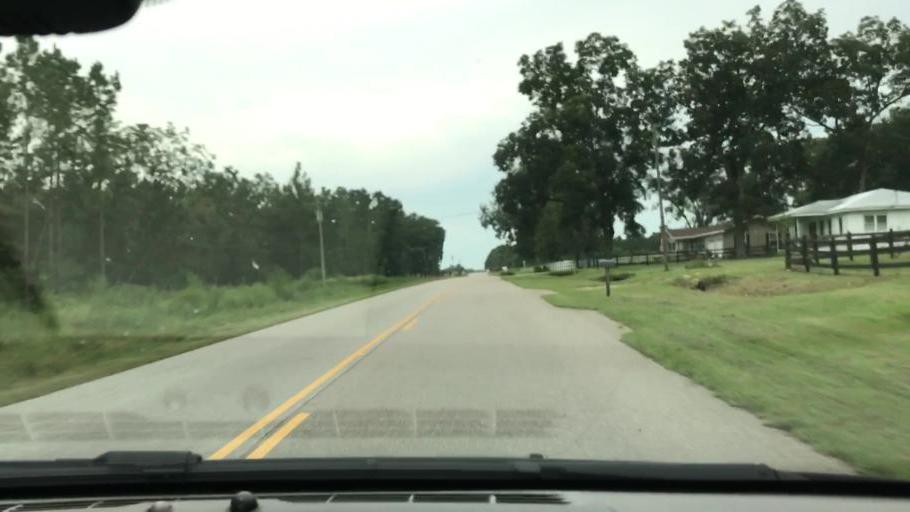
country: US
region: Alabama
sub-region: Houston County
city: Webb
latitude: 31.2642
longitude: -85.1668
